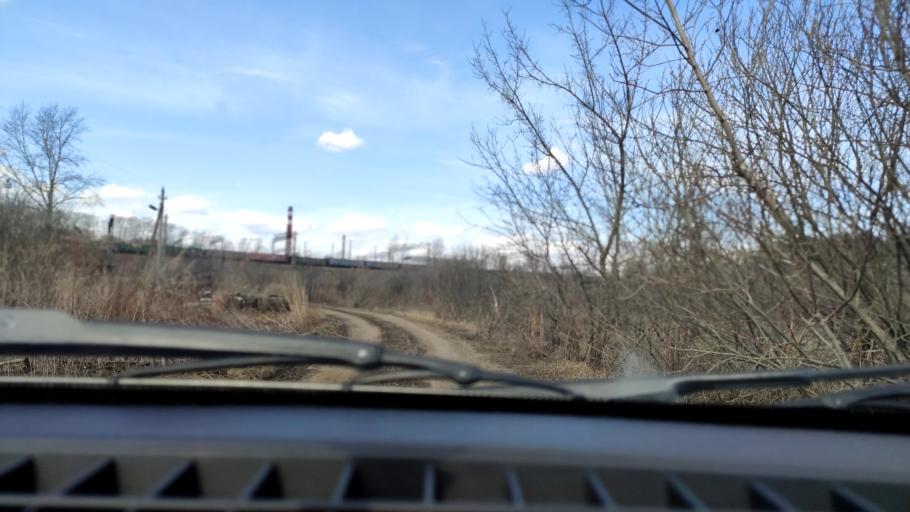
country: RU
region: Bashkortostan
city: Avdon
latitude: 54.6812
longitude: 55.8203
